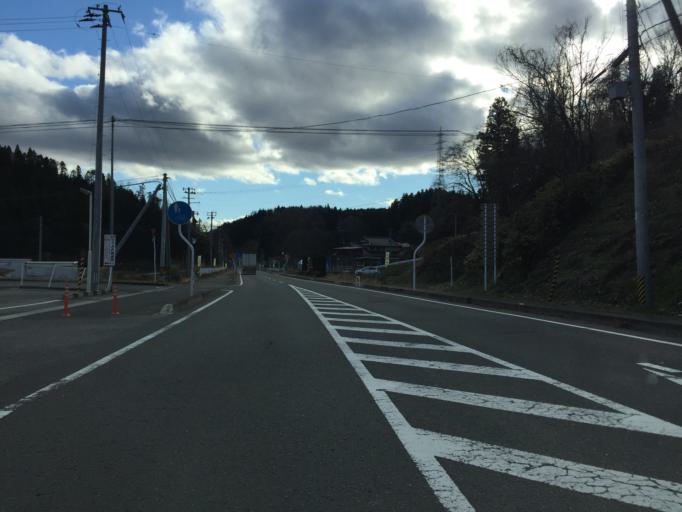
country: JP
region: Fukushima
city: Funehikimachi-funehiki
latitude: 37.5678
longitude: 140.5776
